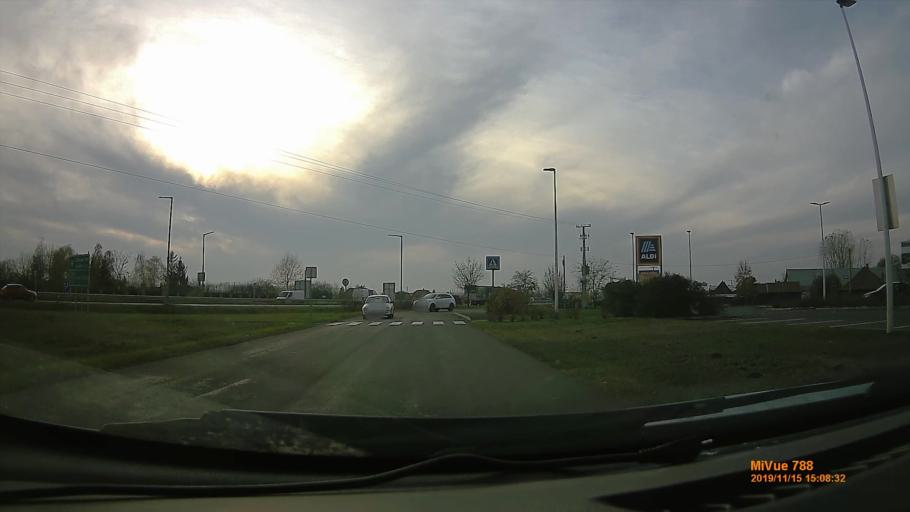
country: HU
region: Bekes
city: Gyula
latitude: 46.6542
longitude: 21.2384
